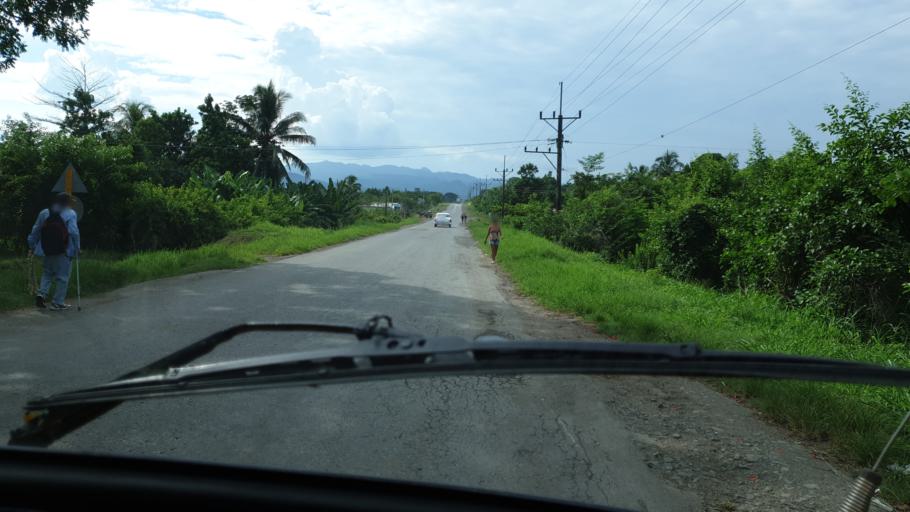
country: CU
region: Cienfuegos
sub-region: Municipio de Cienfuegos
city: Cumanayagua
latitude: 22.0748
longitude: -80.3109
